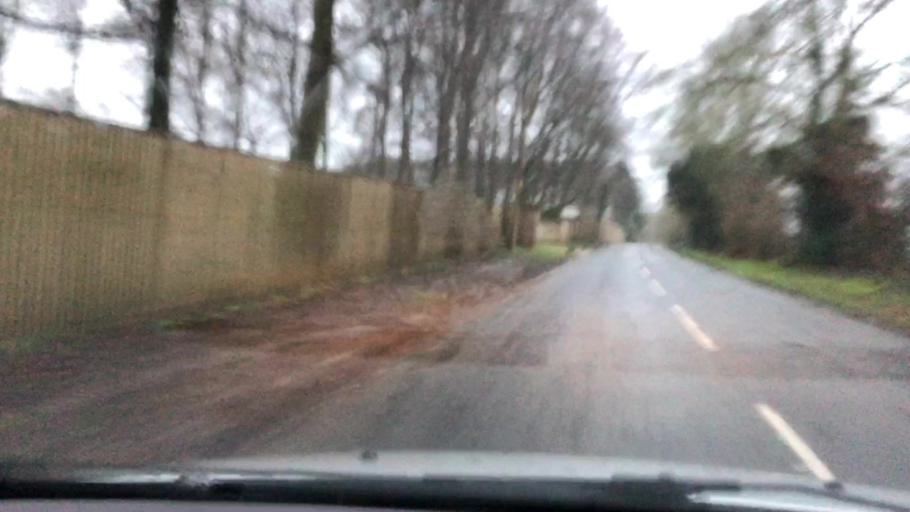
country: GB
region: England
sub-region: Hampshire
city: Alton
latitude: 51.1855
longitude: -0.9951
